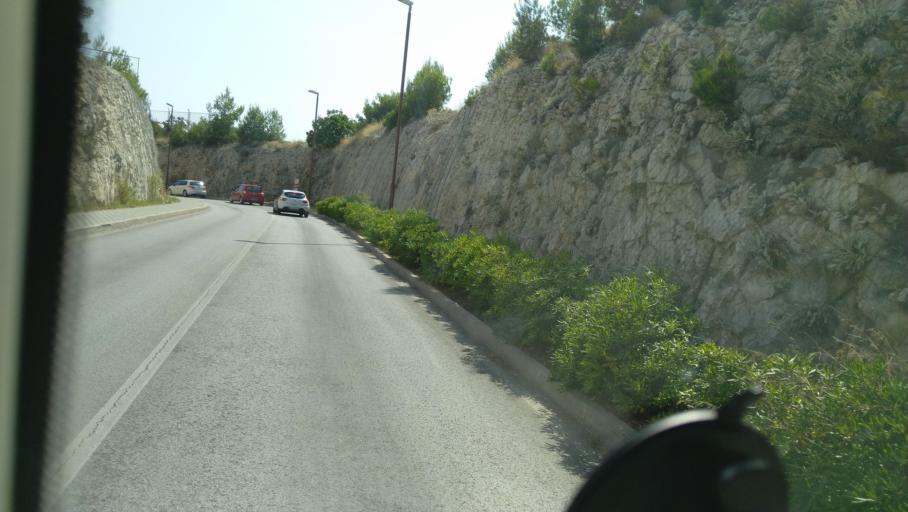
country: HR
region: Sibensko-Kniniska
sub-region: Grad Sibenik
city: Sibenik
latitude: 43.7216
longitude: 15.9069
